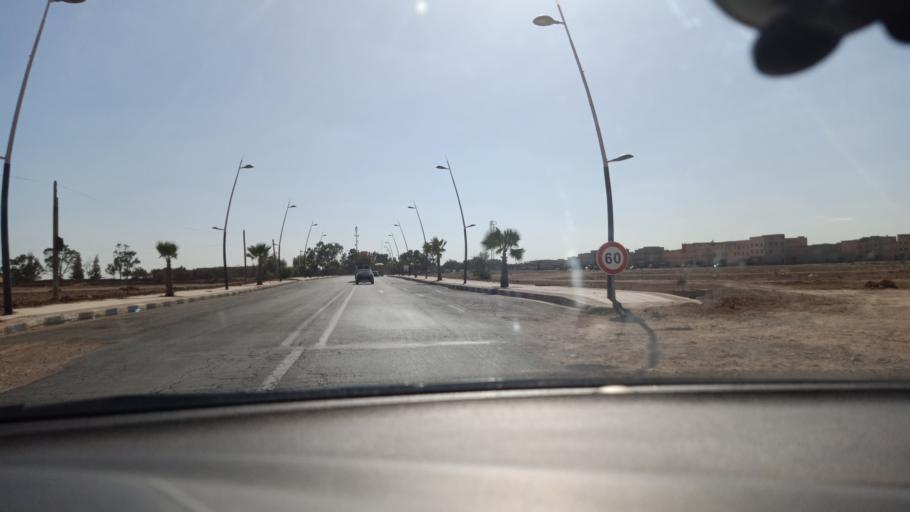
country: MA
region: Doukkala-Abda
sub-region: Safi
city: Youssoufia
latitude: 32.0859
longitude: -8.6193
